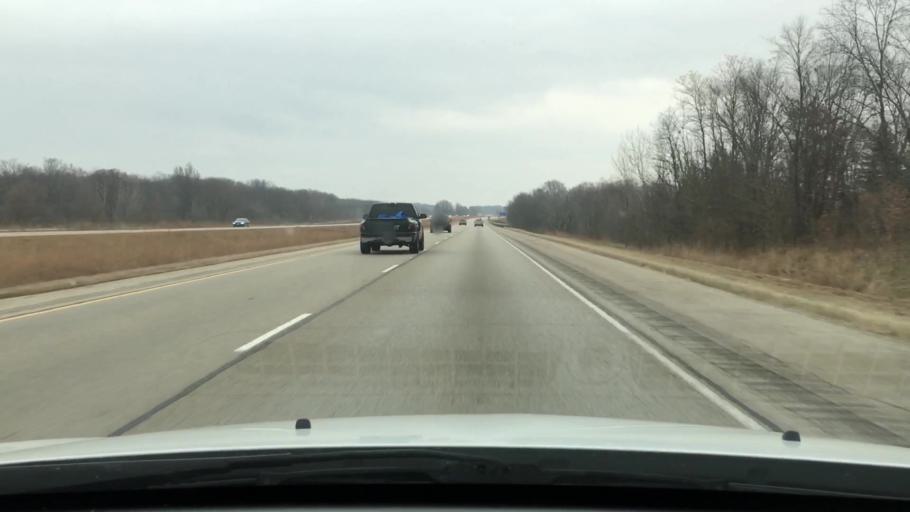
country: US
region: Illinois
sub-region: Logan County
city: Atlanta
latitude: 40.3380
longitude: -89.1410
